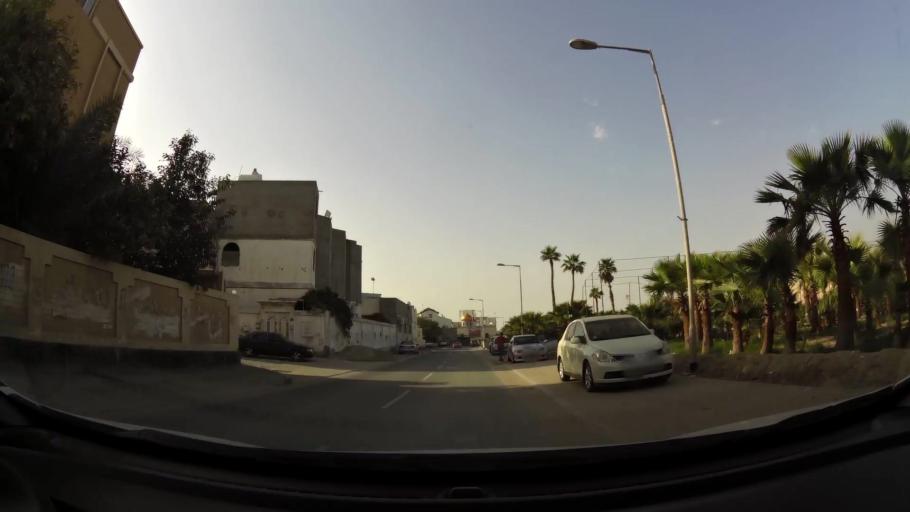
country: BH
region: Manama
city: Jidd Hafs
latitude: 26.2150
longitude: 50.5037
